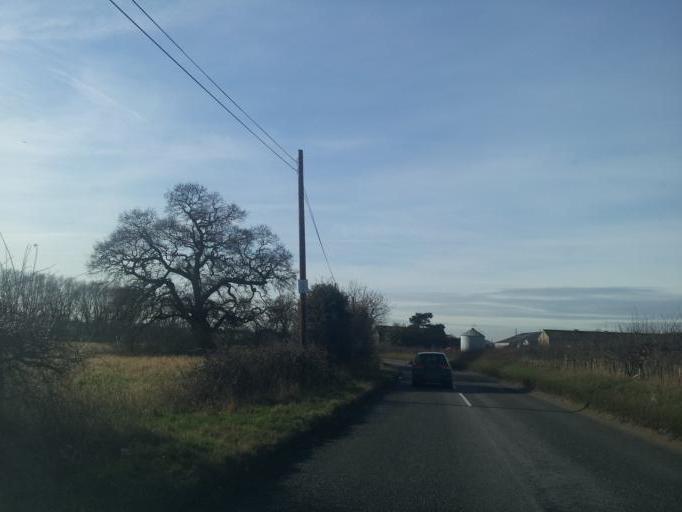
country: GB
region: England
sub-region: Suffolk
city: Wickham Market
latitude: 52.1593
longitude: 1.3159
